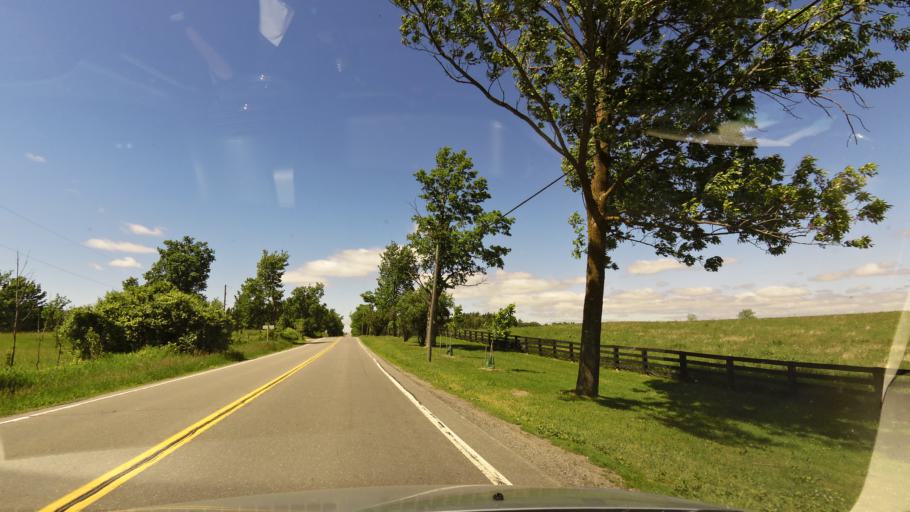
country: CA
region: Ontario
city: Newmarket
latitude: 43.9659
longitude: -79.5385
